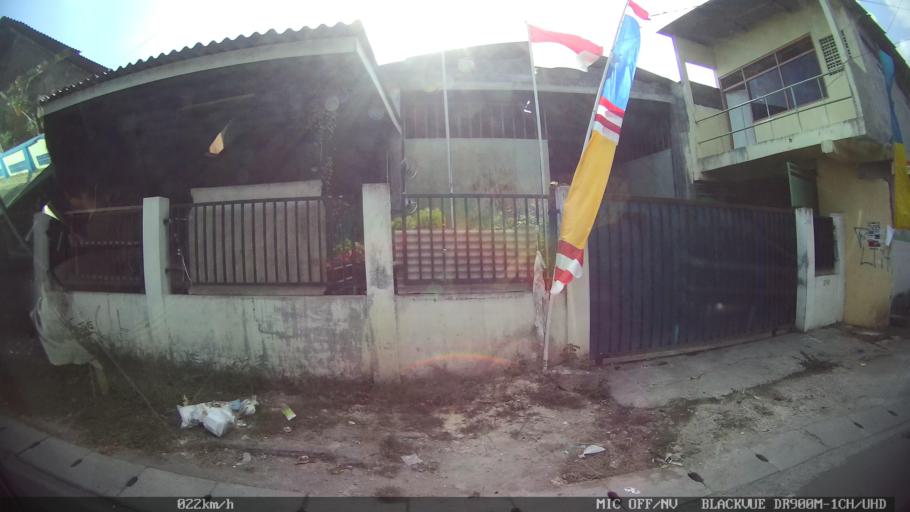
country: ID
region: Daerah Istimewa Yogyakarta
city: Gamping Lor
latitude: -7.7963
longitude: 110.3424
